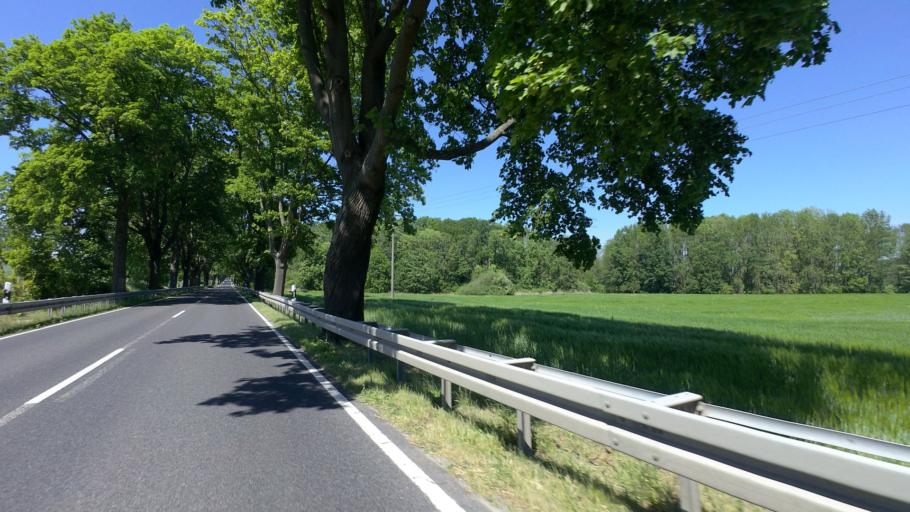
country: DE
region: Brandenburg
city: Lieberose
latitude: 51.9664
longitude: 14.3148
